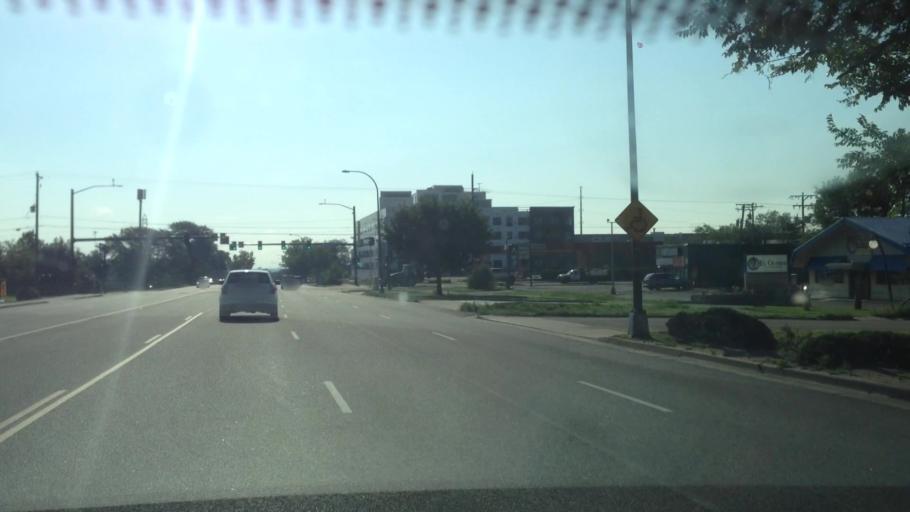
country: US
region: Colorado
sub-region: Jefferson County
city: Lakewood
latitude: 39.7111
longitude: -105.0643
